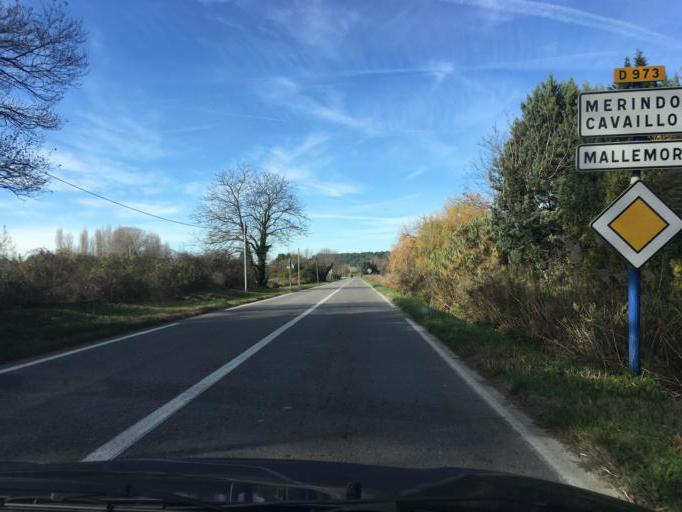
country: FR
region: Provence-Alpes-Cote d'Azur
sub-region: Departement du Vaucluse
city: Lauris
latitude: 43.7463
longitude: 5.3055
